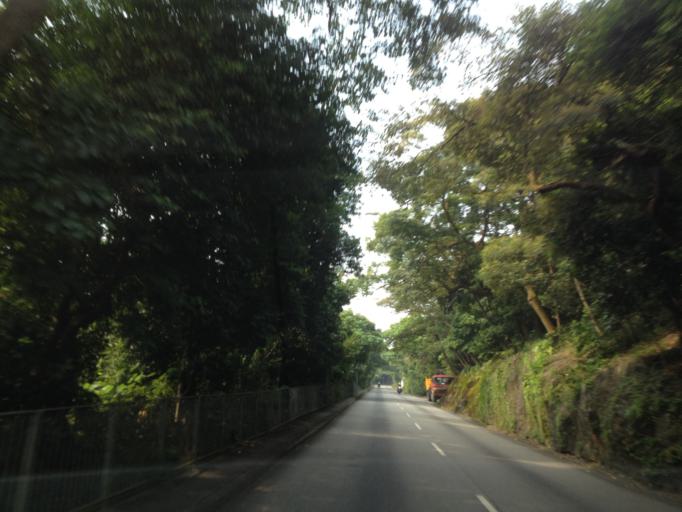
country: HK
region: Wanchai
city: Wan Chai
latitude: 22.2649
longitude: 114.2312
